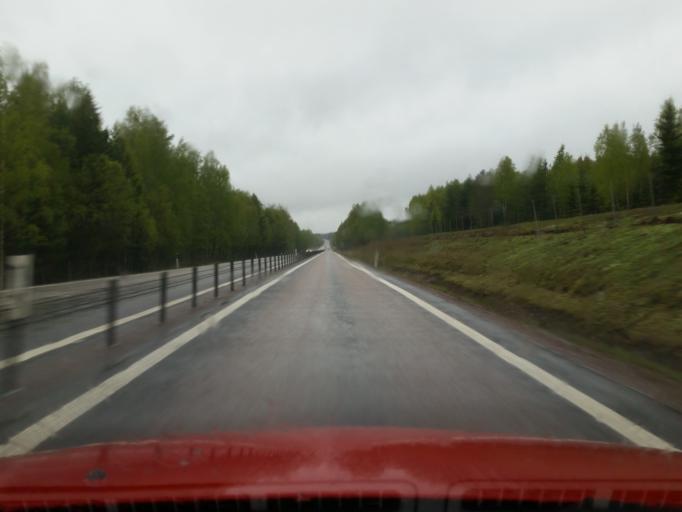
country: SE
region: Dalarna
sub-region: Saters Kommun
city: Saeter
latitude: 60.3759
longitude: 15.6905
